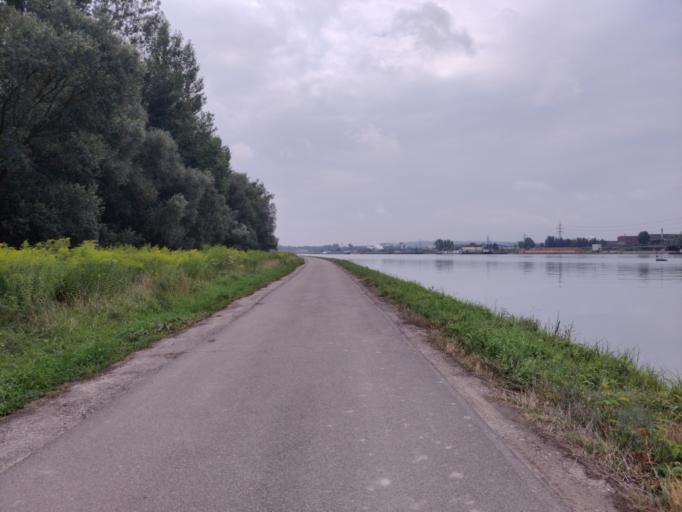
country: AT
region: Upper Austria
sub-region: Politischer Bezirk Urfahr-Umgebung
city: Steyregg
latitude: 48.2862
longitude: 14.3458
